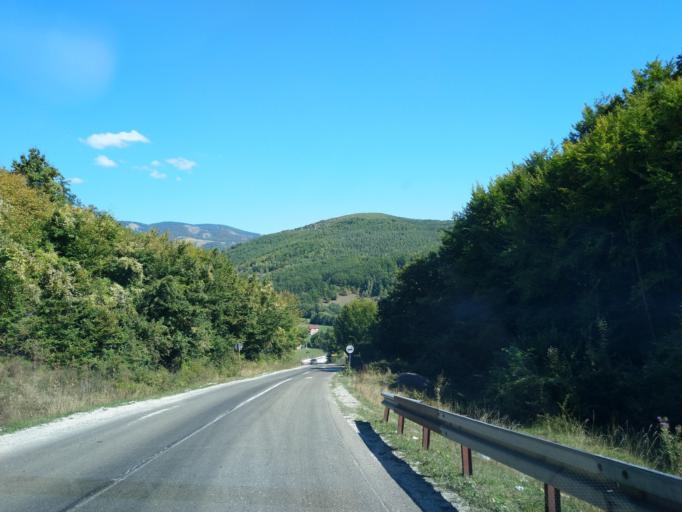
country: RS
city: Sokolovica
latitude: 43.2517
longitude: 20.2538
